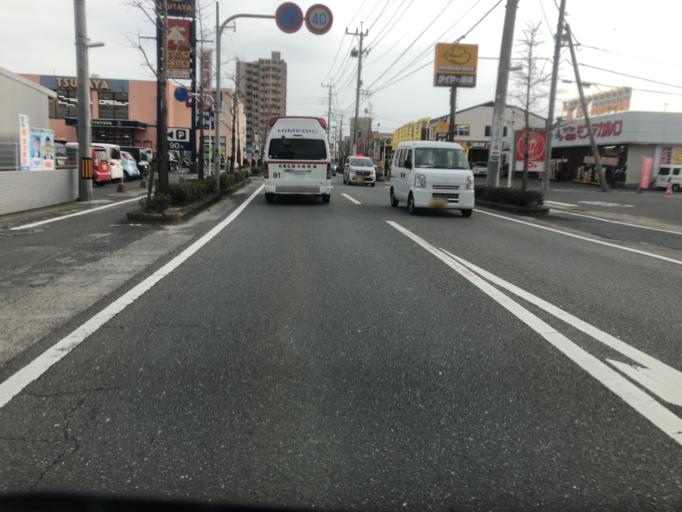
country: JP
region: Saga Prefecture
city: Saga-shi
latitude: 33.2770
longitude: 130.2703
